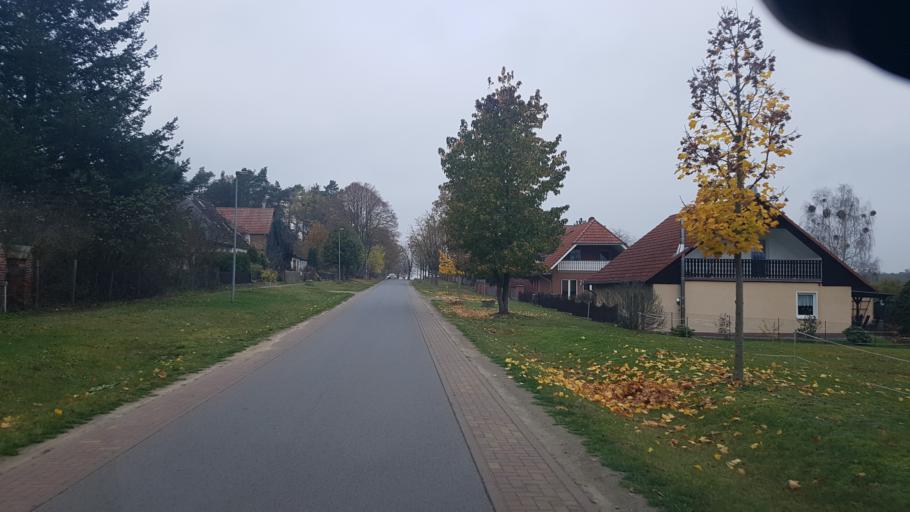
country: DE
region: Brandenburg
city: Sonnenberg
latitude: 52.9368
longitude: 13.0668
